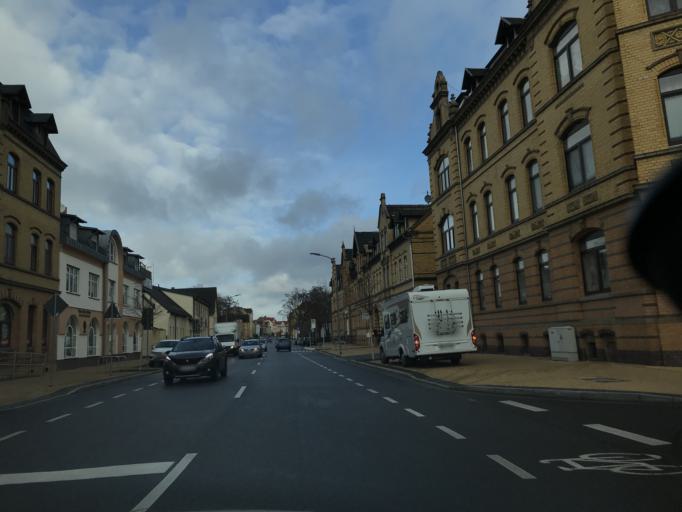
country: DE
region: Saxony
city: Delitzsch
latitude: 51.5259
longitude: 12.3370
